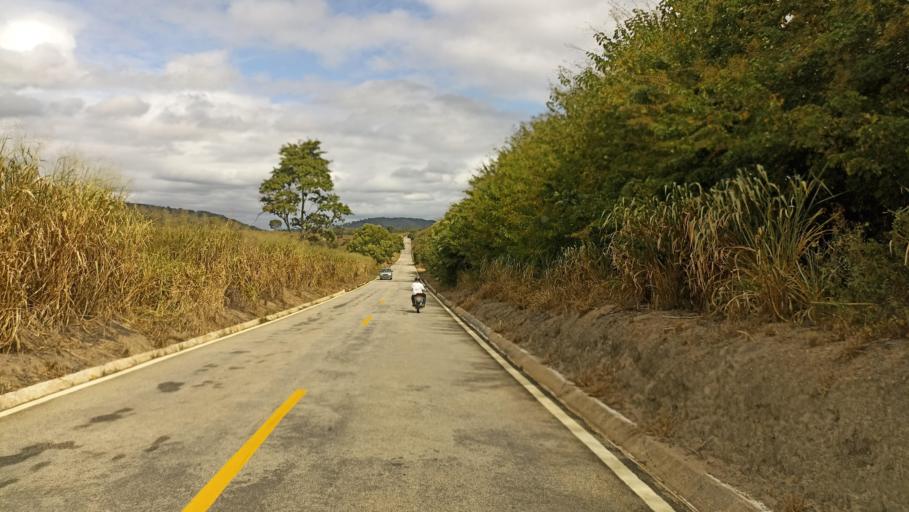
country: BR
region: Minas Gerais
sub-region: Jequitinhonha
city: Jequitinhonha
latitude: -16.5176
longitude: -41.0295
